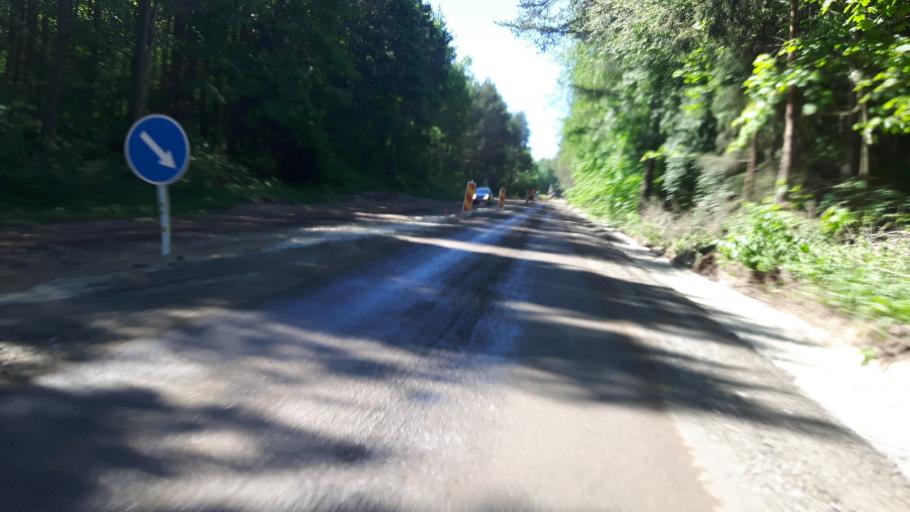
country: EE
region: Ida-Virumaa
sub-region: Narva-Joesuu linn
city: Narva-Joesuu
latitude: 59.4210
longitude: 27.9770
